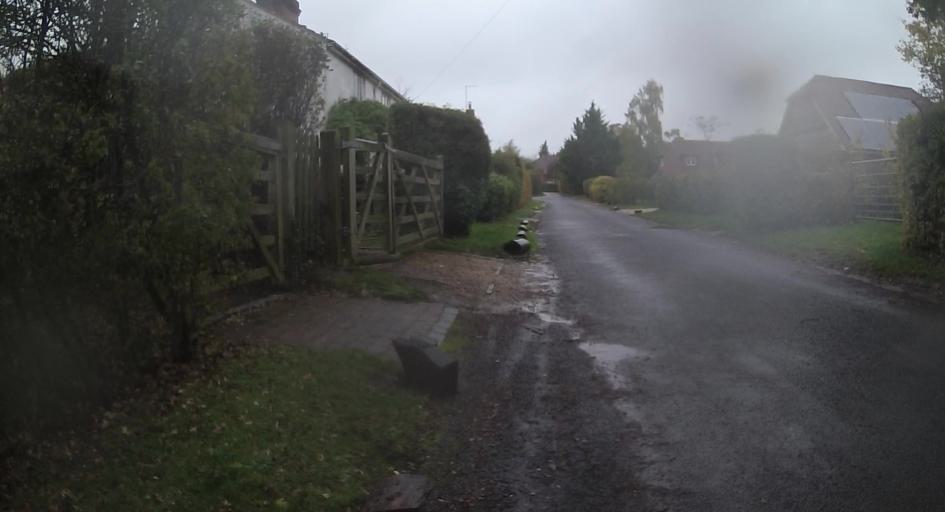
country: GB
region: England
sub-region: Hampshire
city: Kingsley
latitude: 51.1938
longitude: -0.8749
